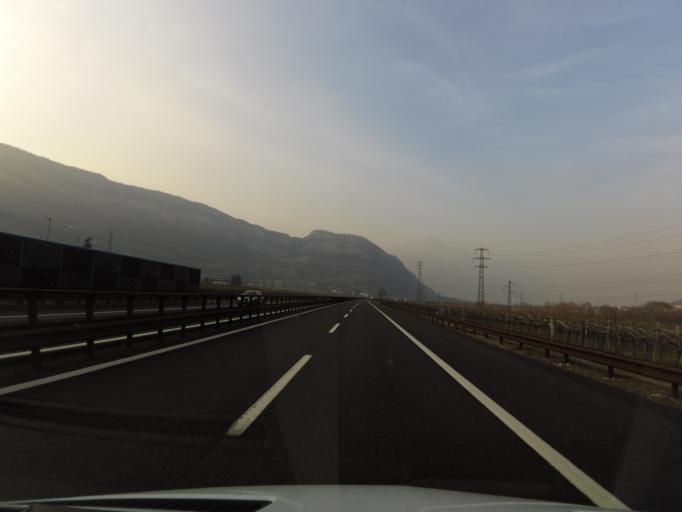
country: IT
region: Trentino-Alto Adige
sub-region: Provincia di Trento
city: Marco
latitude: 45.8160
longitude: 11.0082
